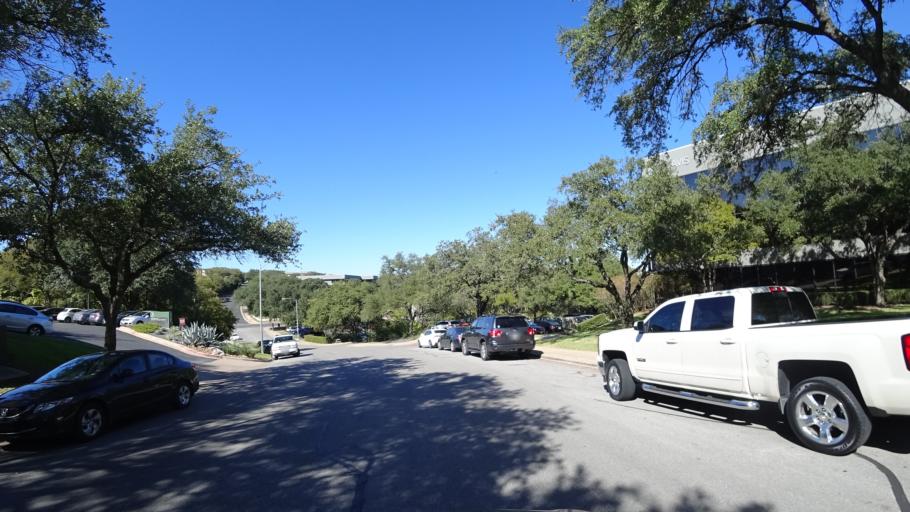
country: US
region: Texas
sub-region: Travis County
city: West Lake Hills
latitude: 30.3597
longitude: -97.7472
